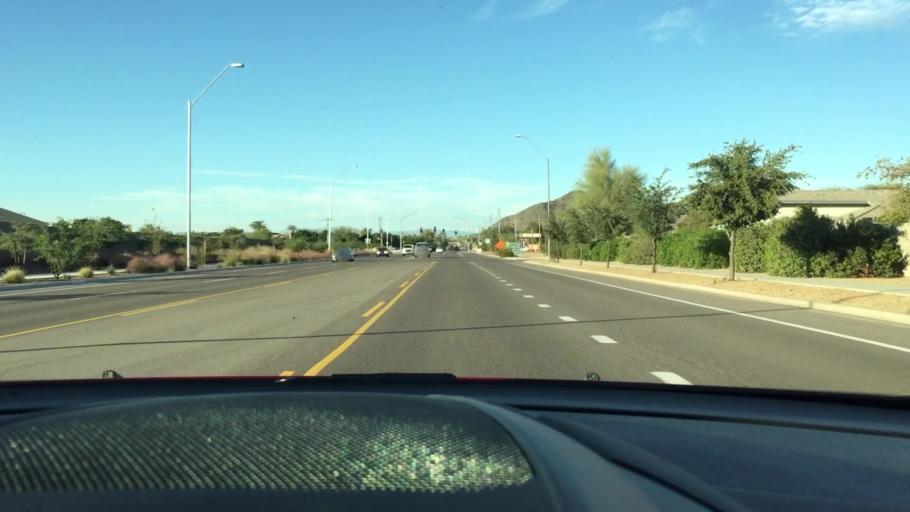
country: US
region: Arizona
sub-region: Maricopa County
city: Sun City West
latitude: 33.6940
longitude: -112.2551
